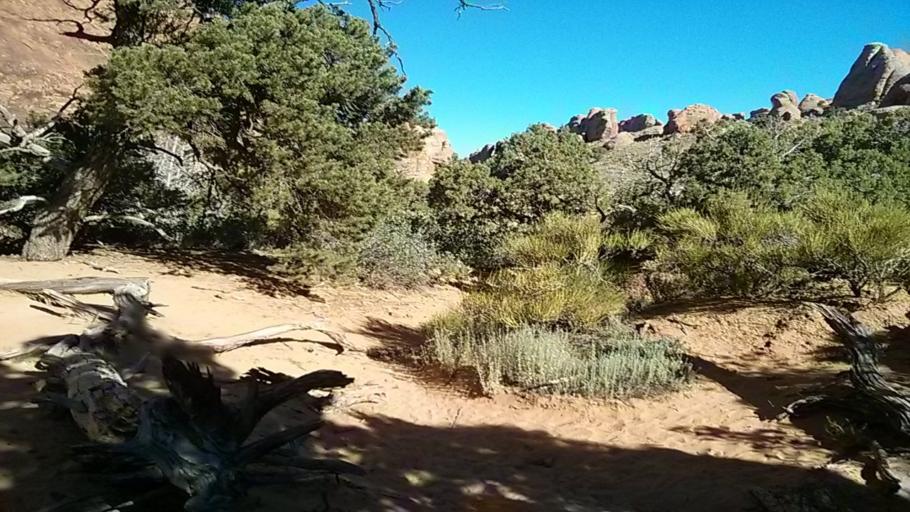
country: US
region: Utah
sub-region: Grand County
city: Moab
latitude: 38.7918
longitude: -109.6066
